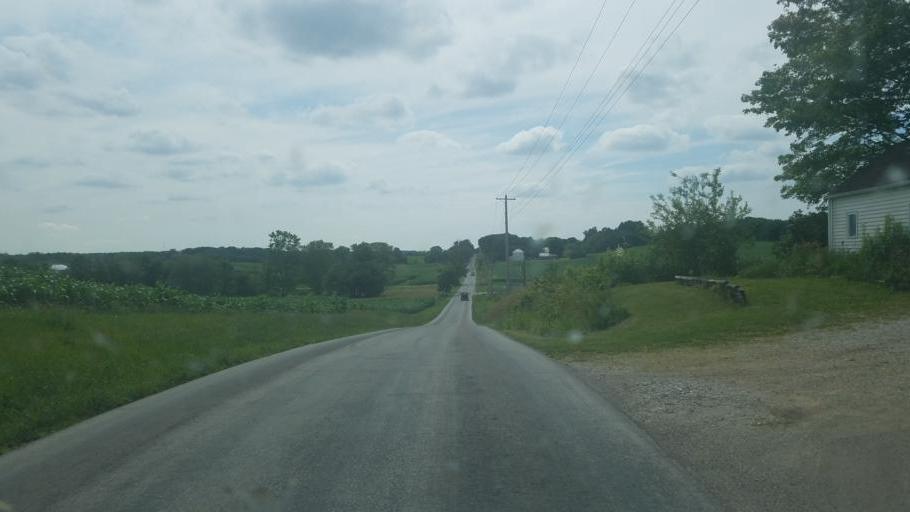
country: US
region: Ohio
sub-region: Knox County
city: Fredericktown
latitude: 40.5235
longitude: -82.6311
